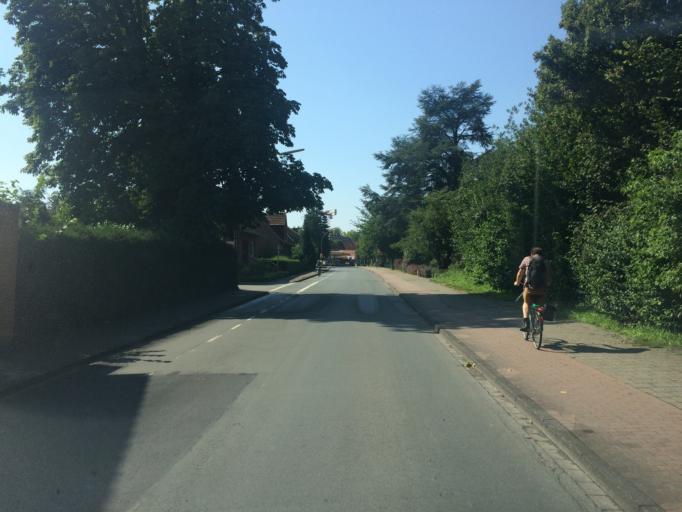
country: DE
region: North Rhine-Westphalia
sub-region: Regierungsbezirk Munster
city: Muenster
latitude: 51.9903
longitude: 7.7010
